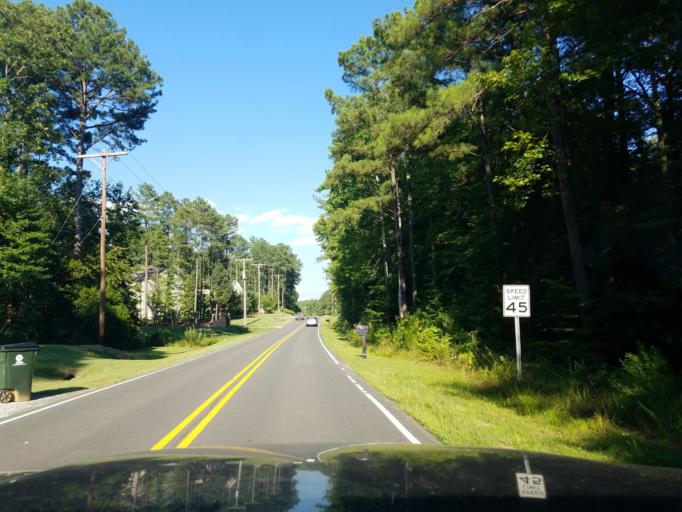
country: US
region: North Carolina
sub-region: Wake County
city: Green Level
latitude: 35.8757
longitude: -78.9299
